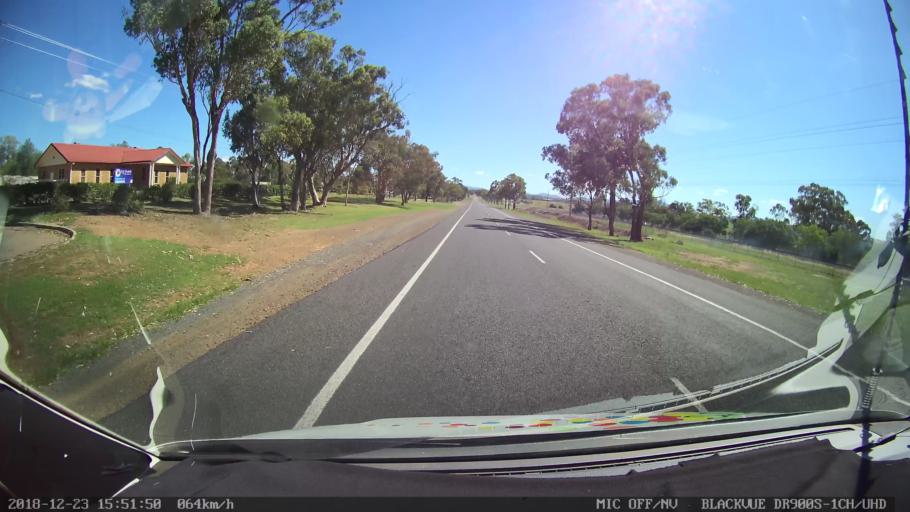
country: AU
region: New South Wales
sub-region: Tamworth Municipality
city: South Tamworth
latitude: -31.1156
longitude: 150.8938
